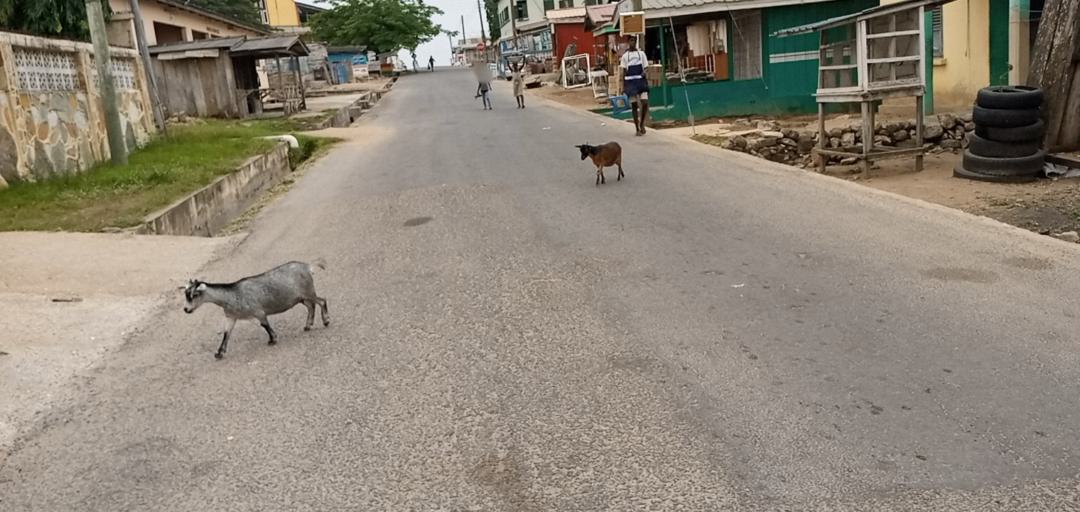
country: GH
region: Central
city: Winneba
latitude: 5.3468
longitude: -0.6243
